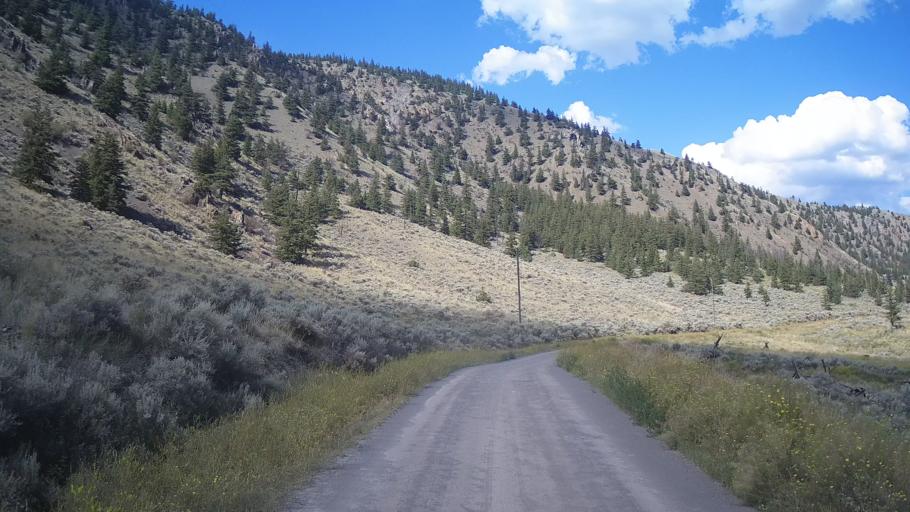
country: CA
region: British Columbia
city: Lillooet
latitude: 51.2182
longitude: -122.0932
